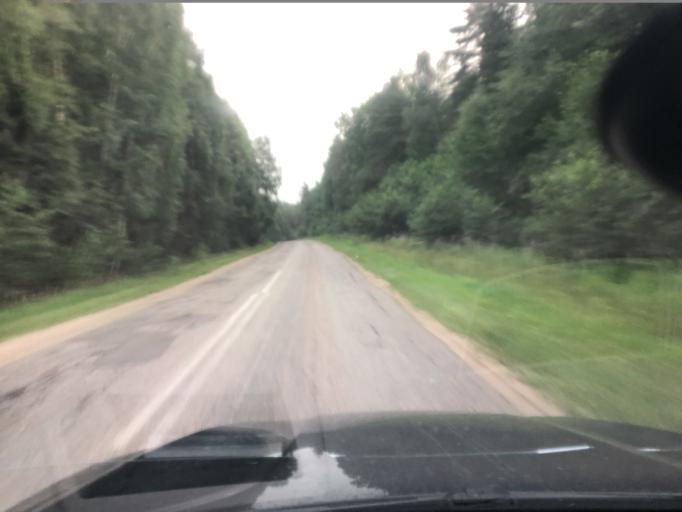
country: RU
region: Jaroslavl
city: Petrovsk
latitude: 57.0001
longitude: 39.0717
